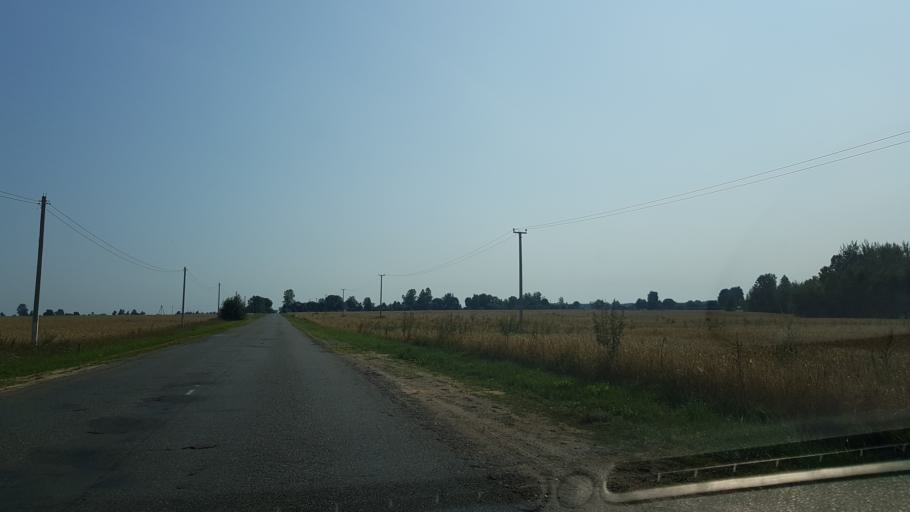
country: BY
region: Mogilev
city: Kirawsk
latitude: 53.2232
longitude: 29.3487
